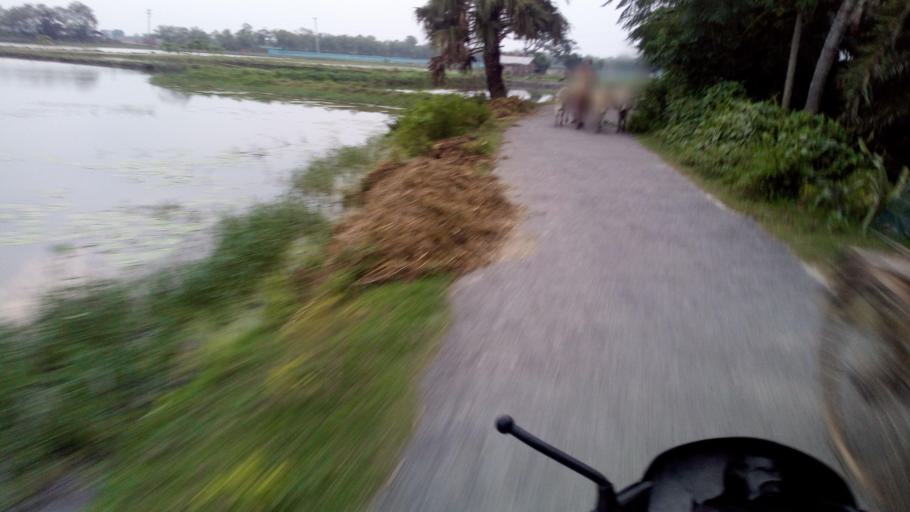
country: BD
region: Khulna
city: Phultala
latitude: 22.7650
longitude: 89.4069
